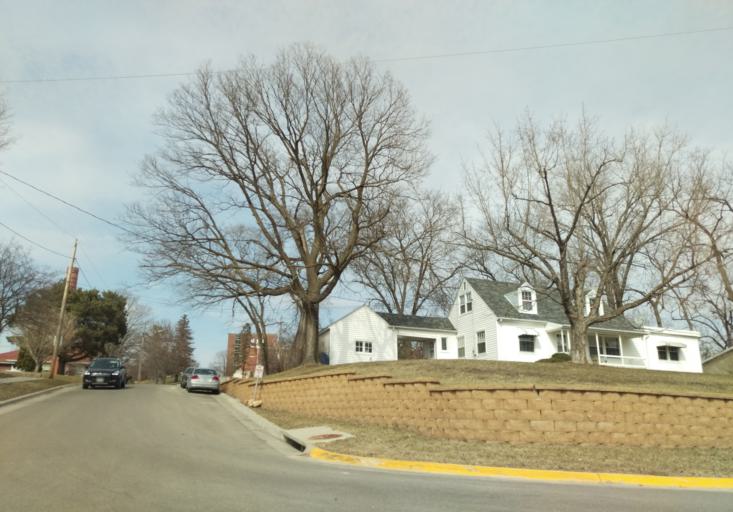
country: US
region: Iowa
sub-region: Winneshiek County
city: Decorah
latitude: 43.3086
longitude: -91.8067
